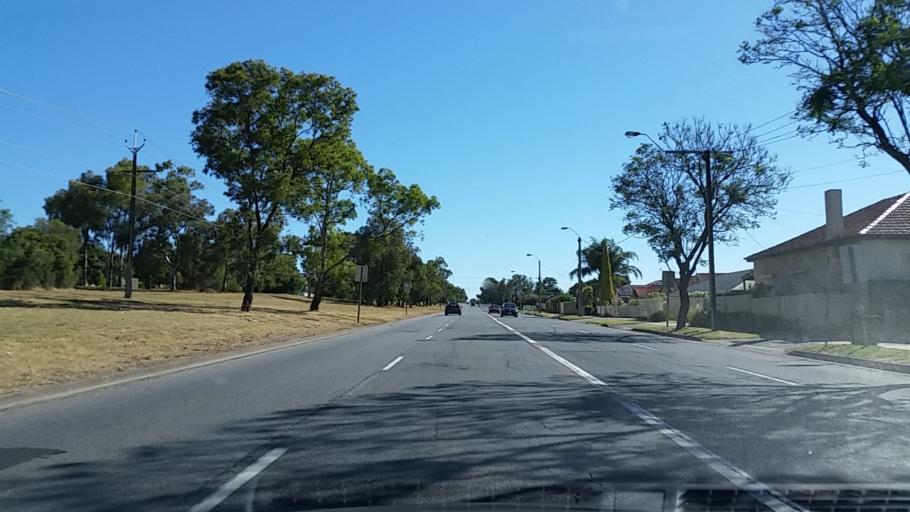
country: AU
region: South Australia
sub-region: Salisbury
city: Ingle Farm
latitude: -34.8287
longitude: 138.6317
